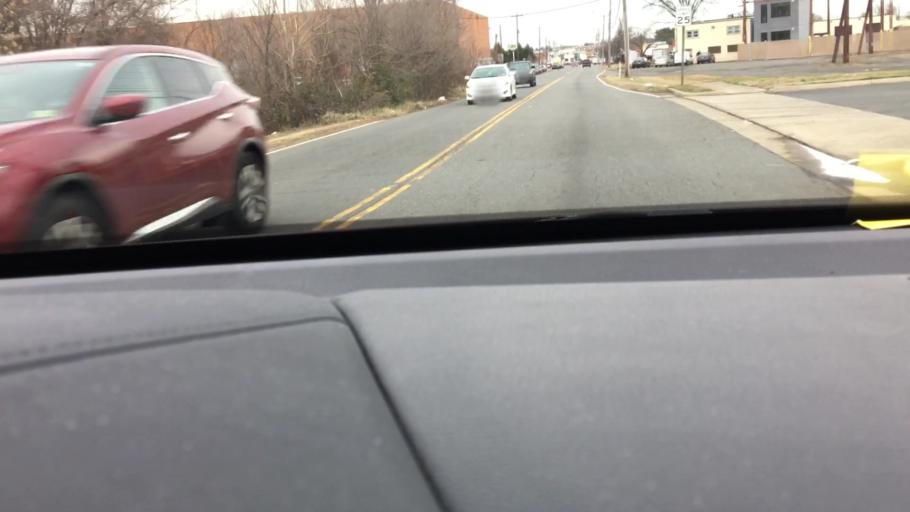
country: US
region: Virginia
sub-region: City of Manassas
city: Manassas
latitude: 38.7552
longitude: -77.4581
